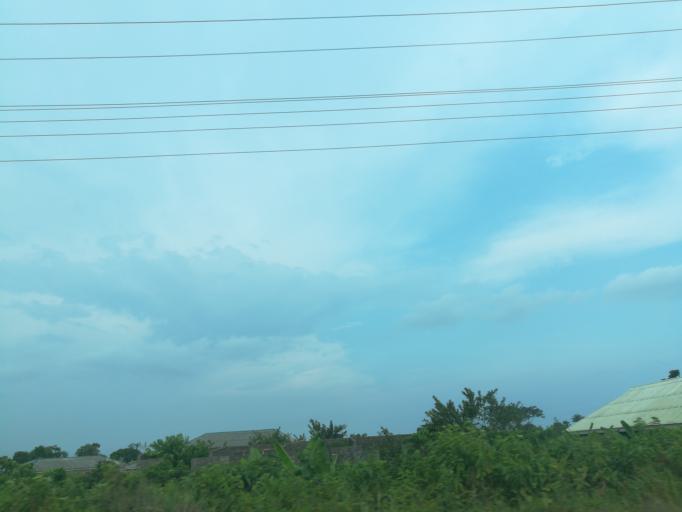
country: NG
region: Lagos
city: Ikorodu
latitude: 6.6426
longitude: 3.6709
